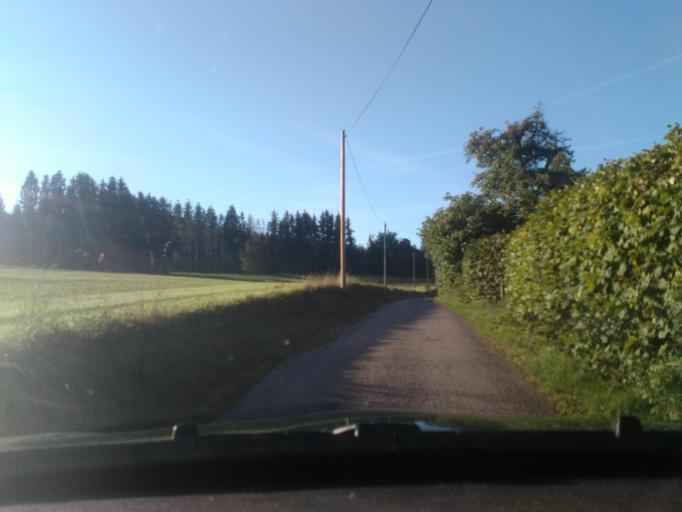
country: FR
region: Lorraine
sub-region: Departement des Vosges
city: Senones
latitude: 48.3745
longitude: 7.0340
